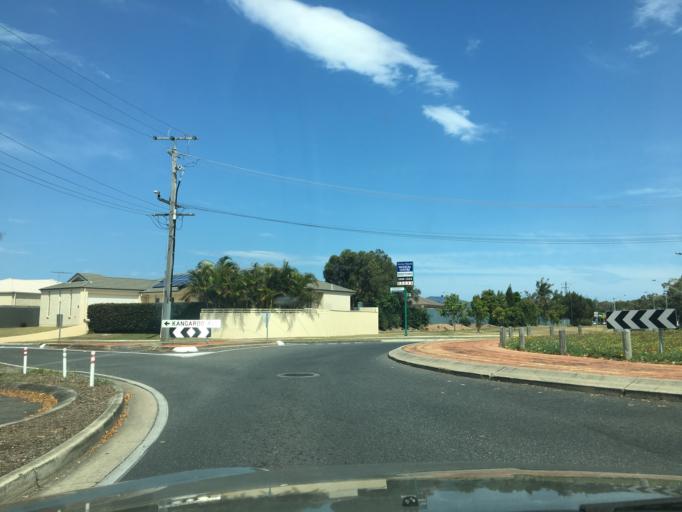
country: AU
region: Queensland
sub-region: Moreton Bay
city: Bongaree
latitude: -27.0741
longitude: 153.1636
